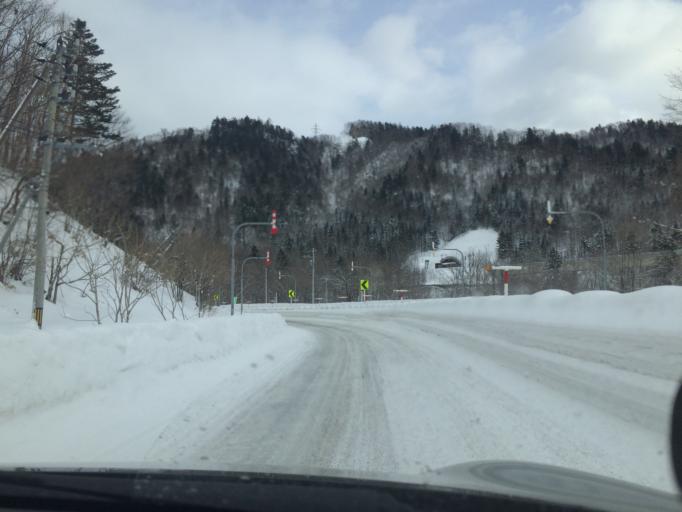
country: JP
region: Hokkaido
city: Shimo-furano
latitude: 43.0469
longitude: 142.4800
